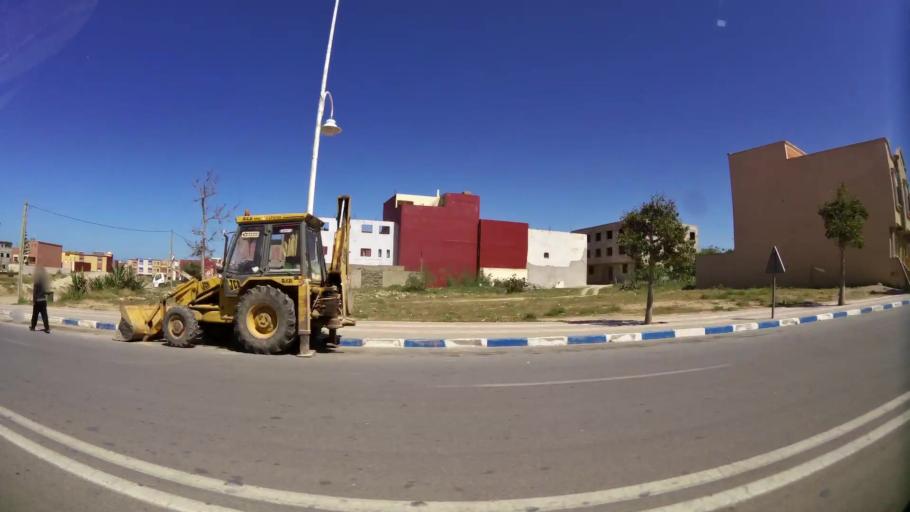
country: MA
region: Oriental
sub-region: Berkane-Taourirt
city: Madagh
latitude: 35.1352
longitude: -2.4243
